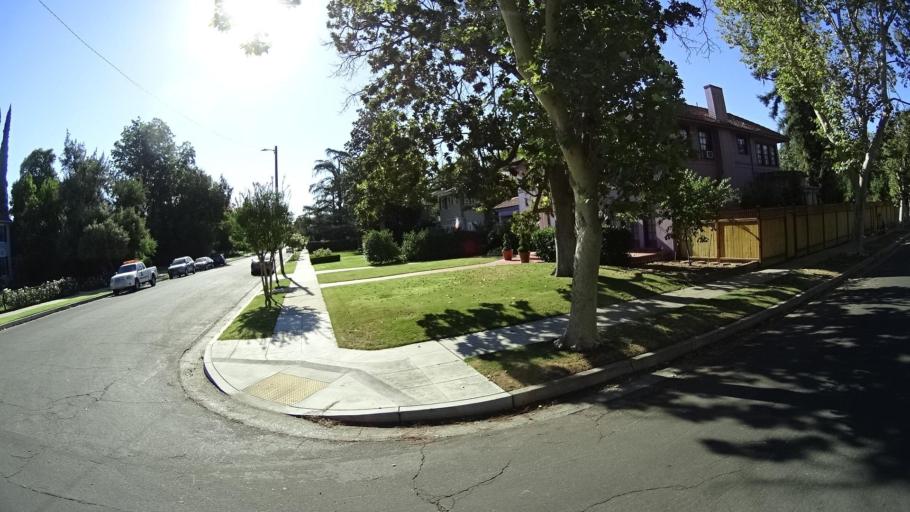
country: US
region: California
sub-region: Fresno County
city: Fresno
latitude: 36.7631
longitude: -119.8046
